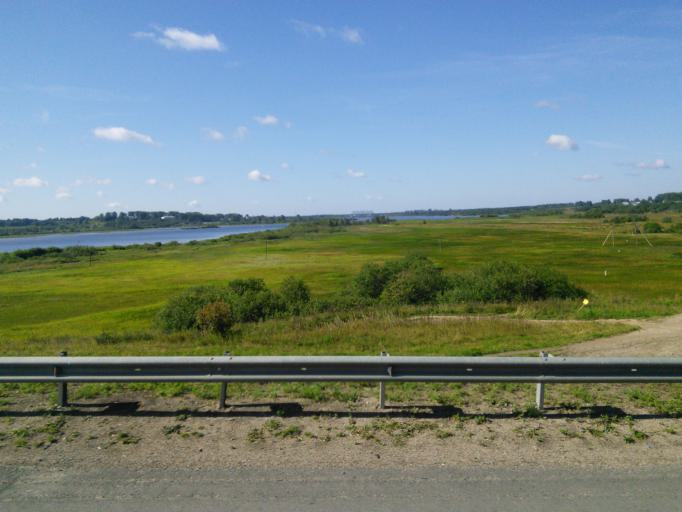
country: RU
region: Vologda
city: Sheksna
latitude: 59.2157
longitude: 38.4907
